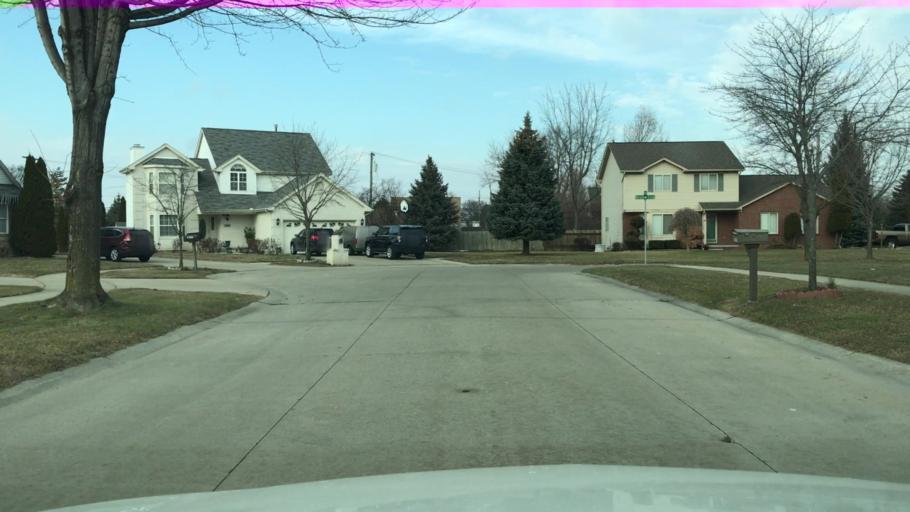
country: US
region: Michigan
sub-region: Macomb County
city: Sterling Heights
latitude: 42.5634
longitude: -83.0549
